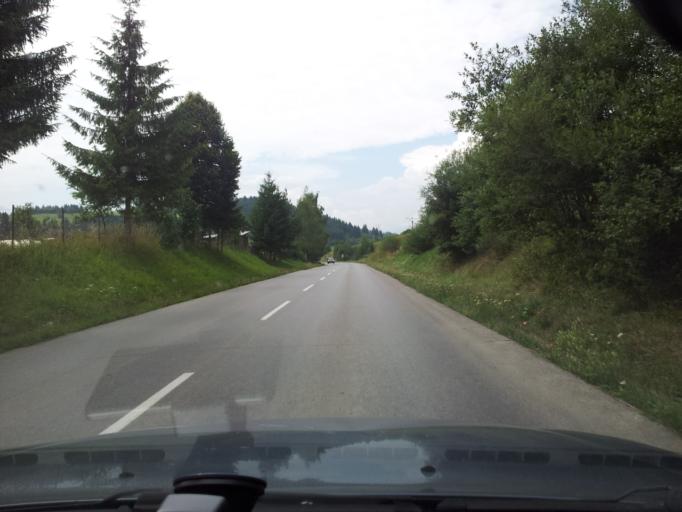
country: SK
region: Zilinsky
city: Namestovo
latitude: 49.3794
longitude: 19.3413
